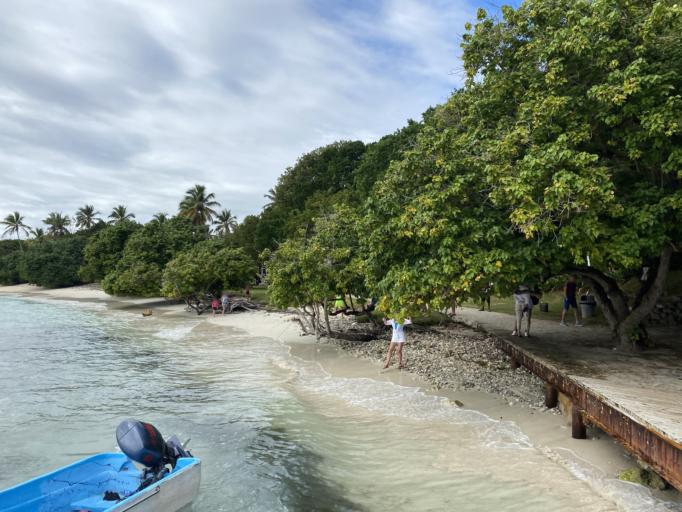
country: DO
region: Samana
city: Samana
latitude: 19.1663
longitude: -69.2779
